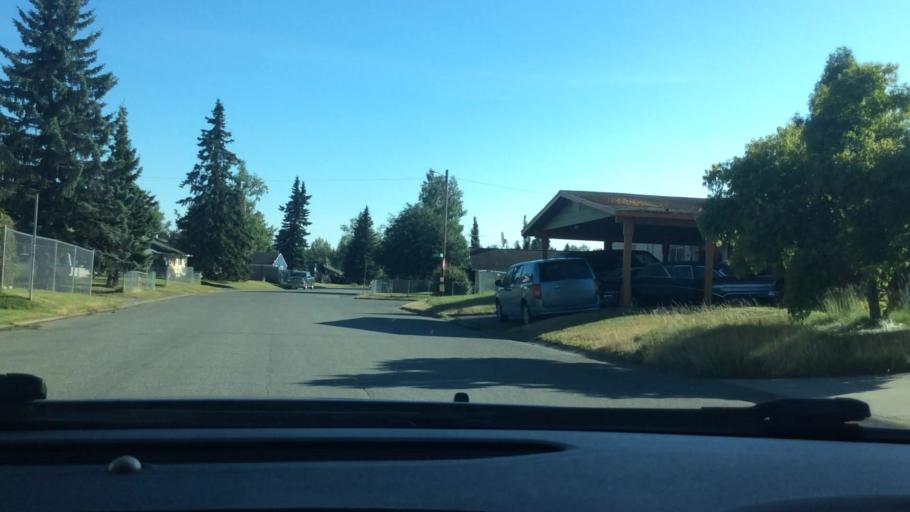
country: US
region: Alaska
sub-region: Anchorage Municipality
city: Anchorage
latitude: 61.2063
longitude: -149.7707
